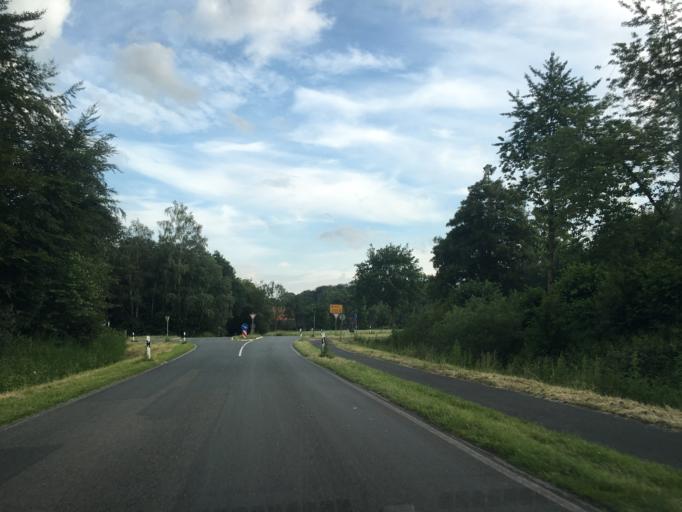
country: DE
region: North Rhine-Westphalia
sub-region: Regierungsbezirk Munster
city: Havixbeck
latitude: 51.9926
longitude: 7.4670
